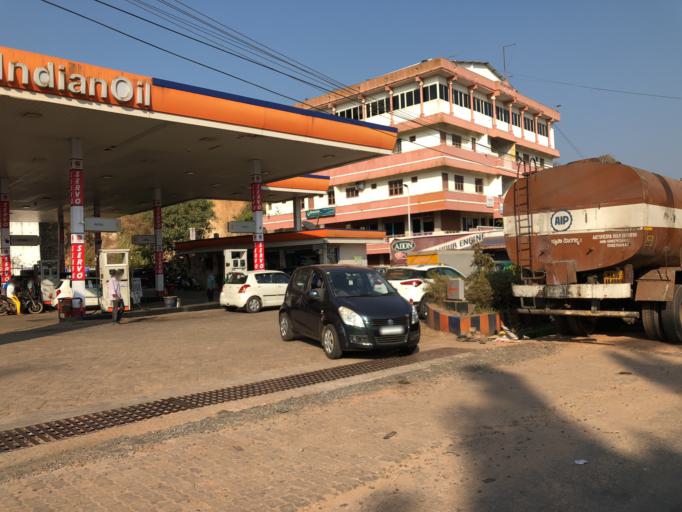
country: IN
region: Karnataka
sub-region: Dakshina Kannada
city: Mangalore
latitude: 12.8691
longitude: 74.8679
